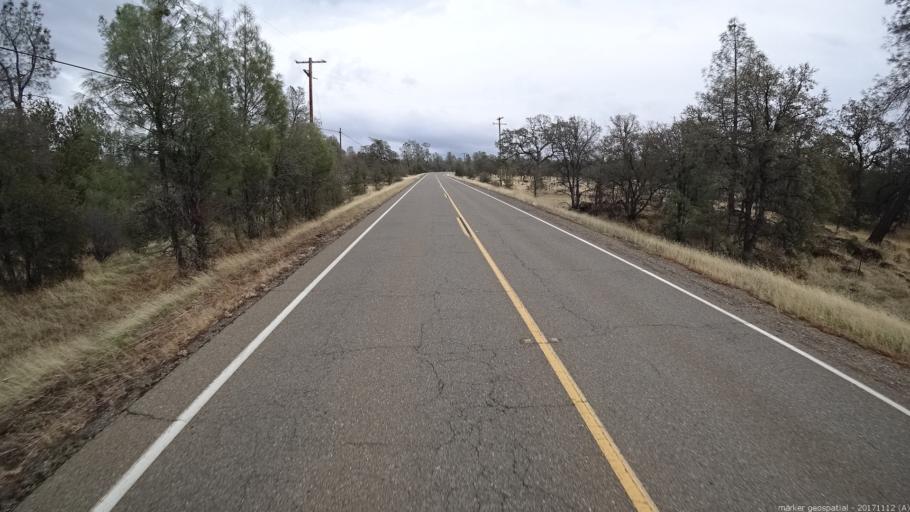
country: US
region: California
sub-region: Shasta County
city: Palo Cedro
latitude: 40.4876
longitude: -122.1229
